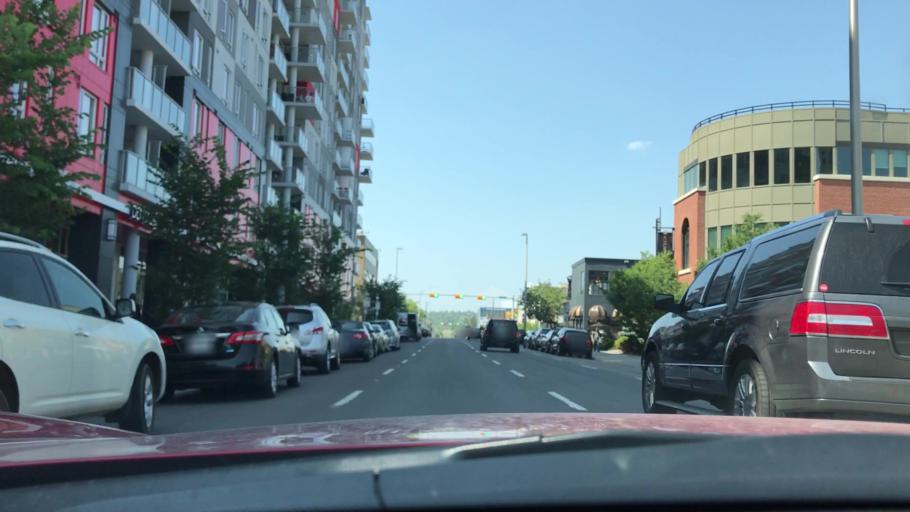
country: CA
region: Alberta
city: Calgary
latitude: 51.0431
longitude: -114.0896
